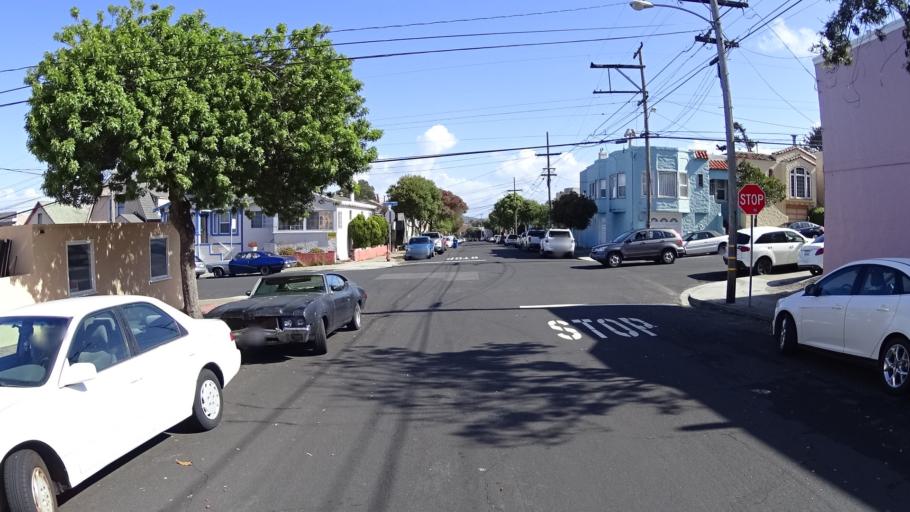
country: US
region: California
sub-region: San Mateo County
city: Daly City
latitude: 37.7054
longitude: -122.4559
